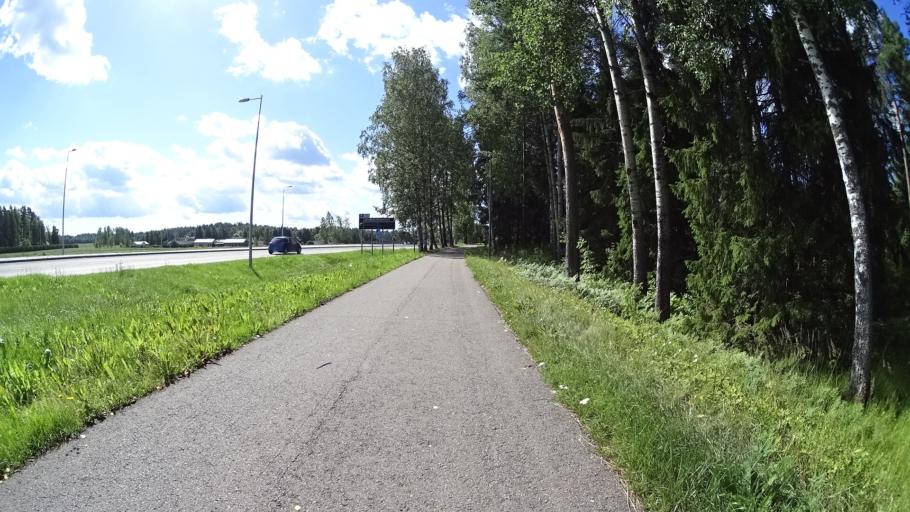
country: FI
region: Uusimaa
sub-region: Helsinki
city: Jaervenpaeae
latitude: 60.4549
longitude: 25.0824
